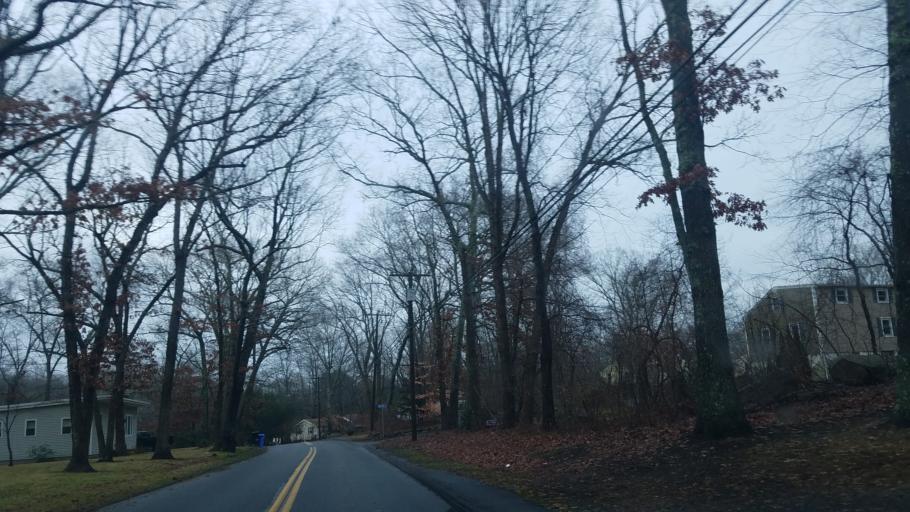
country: US
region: Connecticut
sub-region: Middlesex County
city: Clinton
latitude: 41.3057
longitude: -72.5334
